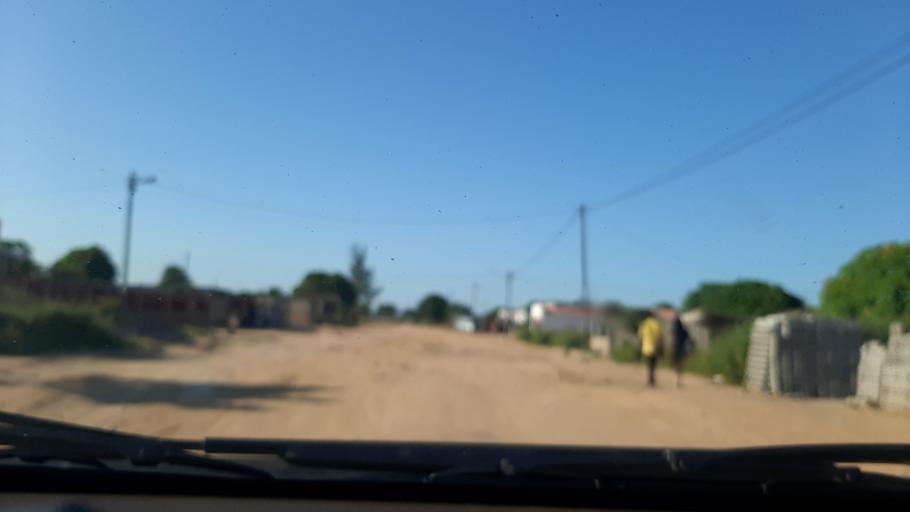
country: MZ
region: Maputo City
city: Maputo
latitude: -25.8054
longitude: 32.5468
